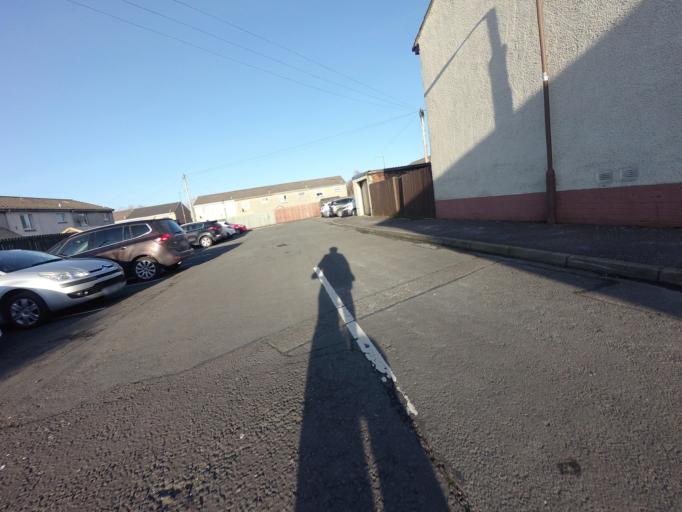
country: GB
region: Scotland
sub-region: West Lothian
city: West Calder
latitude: 55.8639
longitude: -3.5469
